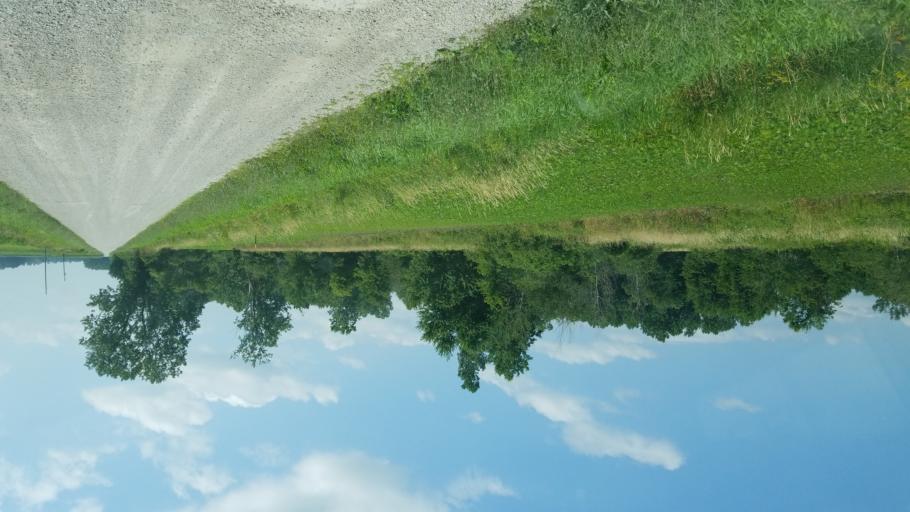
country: US
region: Ohio
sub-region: Huron County
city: Willard
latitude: 41.0065
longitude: -82.7806
